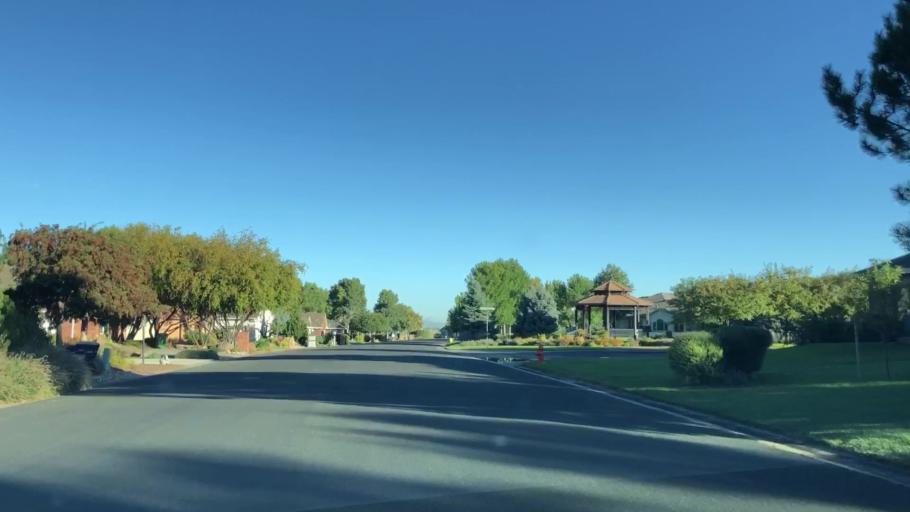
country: US
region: Colorado
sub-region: Larimer County
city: Loveland
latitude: 40.4309
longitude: -105.0234
